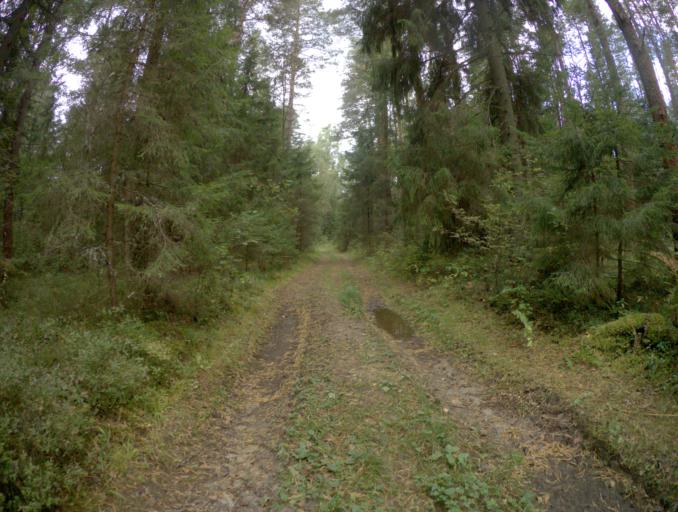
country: RU
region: Vladimir
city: Golovino
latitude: 55.8893
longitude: 40.4364
